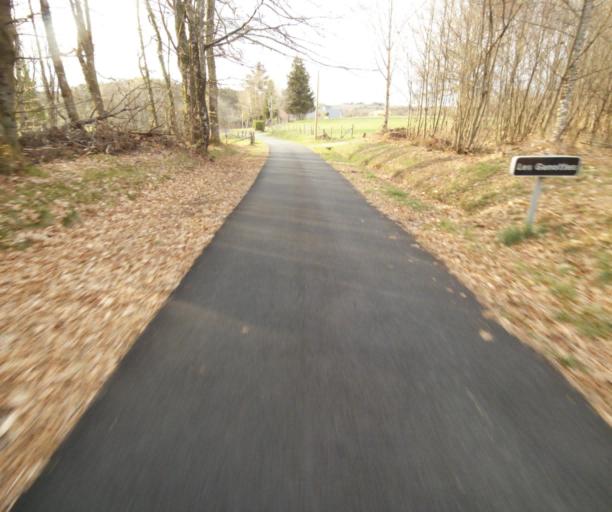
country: FR
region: Limousin
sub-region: Departement de la Correze
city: Argentat
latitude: 45.2202
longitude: 1.9550
